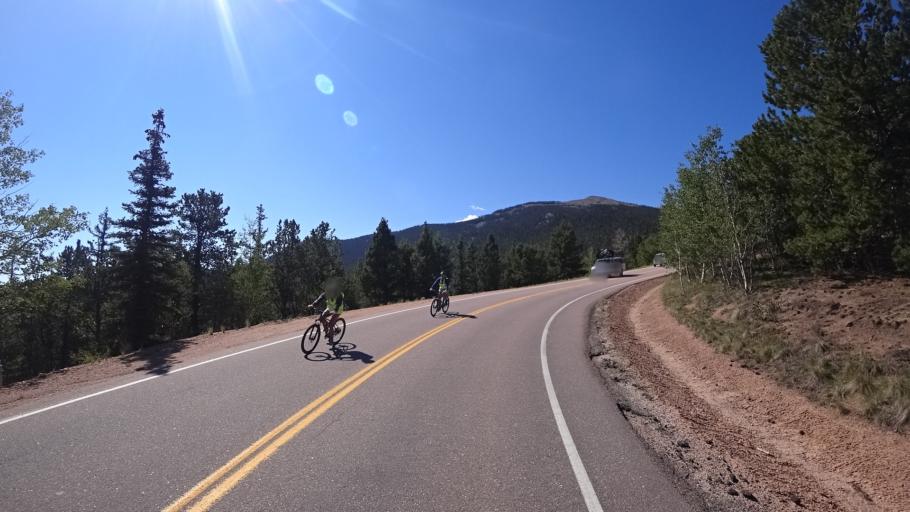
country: US
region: Colorado
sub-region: El Paso County
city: Cascade-Chipita Park
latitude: 38.9038
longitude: -105.0608
